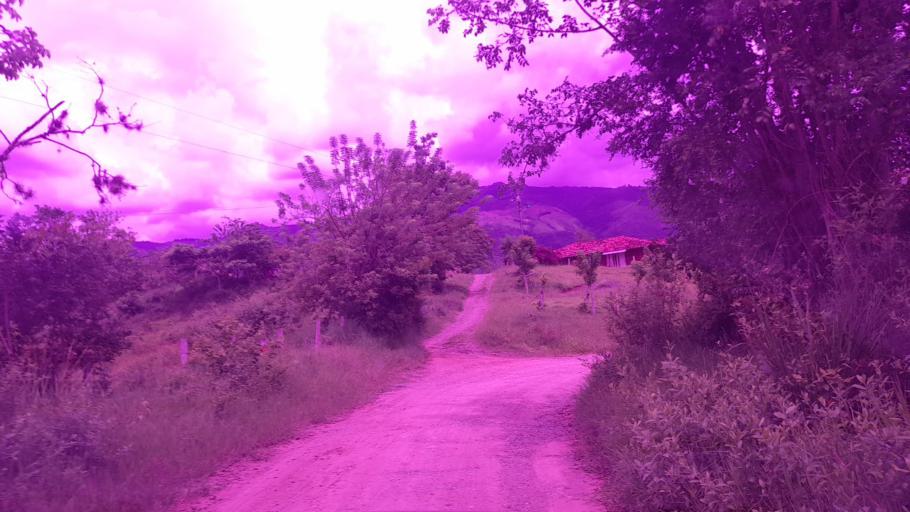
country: CO
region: Valle del Cauca
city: Andalucia
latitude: 4.1675
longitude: -76.0922
